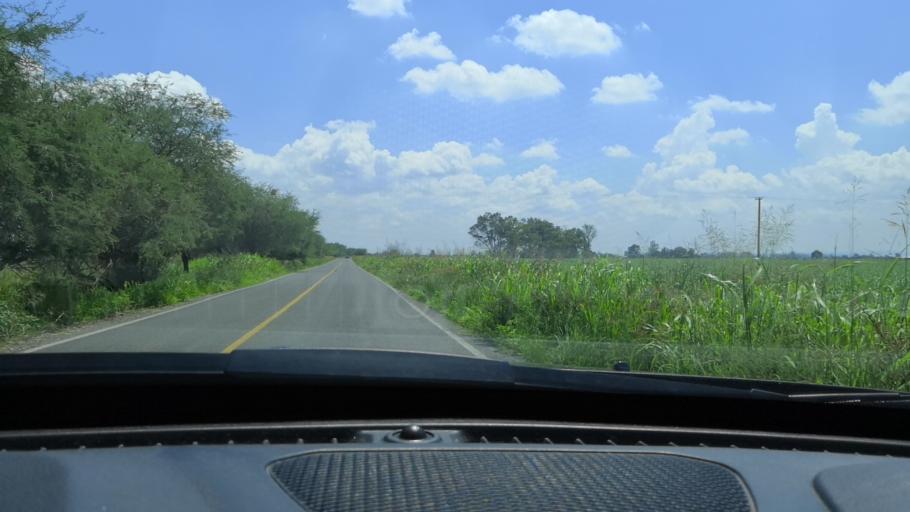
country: MX
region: Guanajuato
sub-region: Silao de la Victoria
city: El Refugio de los Sauces
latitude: 20.9571
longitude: -101.5924
